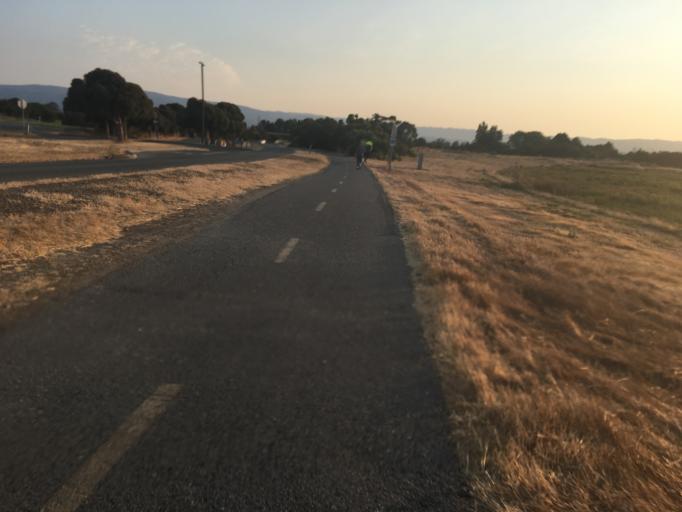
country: US
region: California
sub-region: Santa Clara County
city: Mountain View
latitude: 37.4337
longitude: -122.0824
